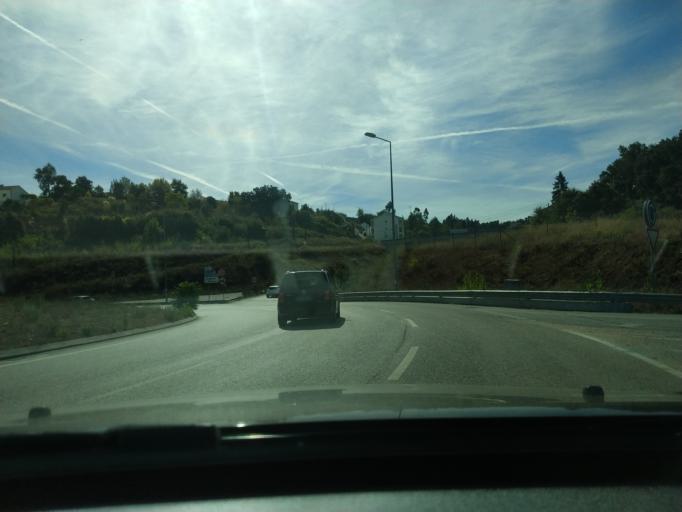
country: PT
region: Coimbra
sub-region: Coimbra
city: Coimbra
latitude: 40.2144
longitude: -8.4466
